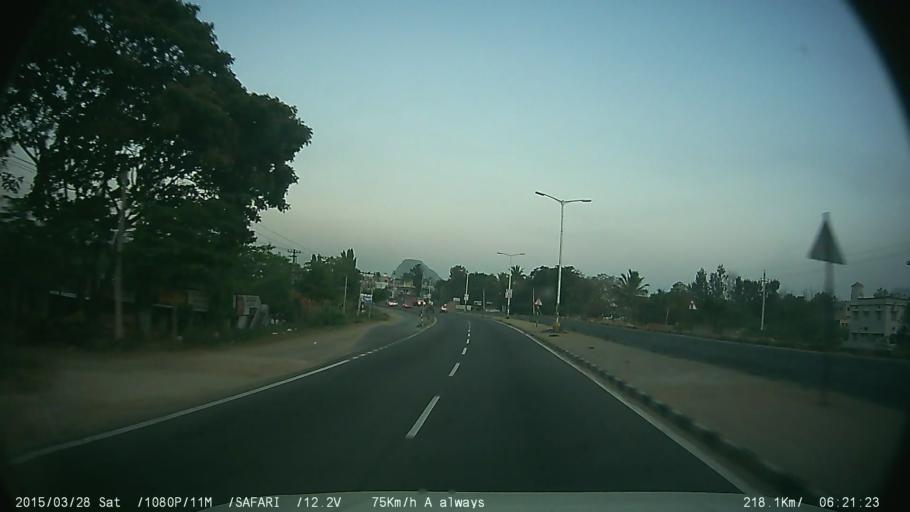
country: IN
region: Karnataka
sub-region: Ramanagara
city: Ramanagaram
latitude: 12.7302
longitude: 77.2804
